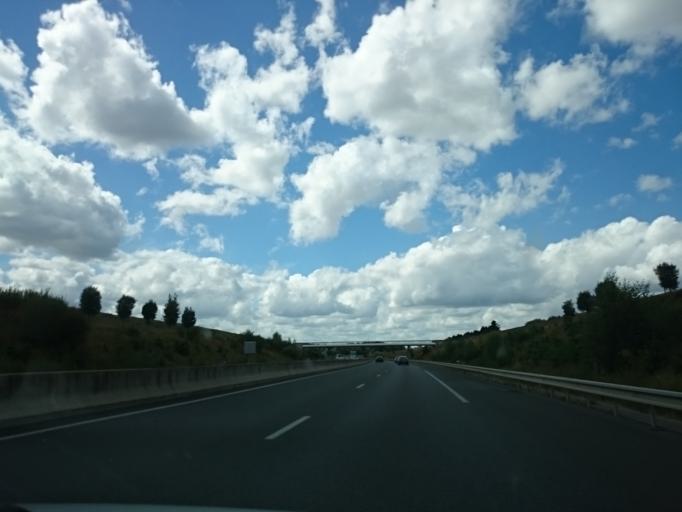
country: FR
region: Pays de la Loire
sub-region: Departement de Maine-et-Loire
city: Avrille
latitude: 47.4940
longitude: -0.6007
